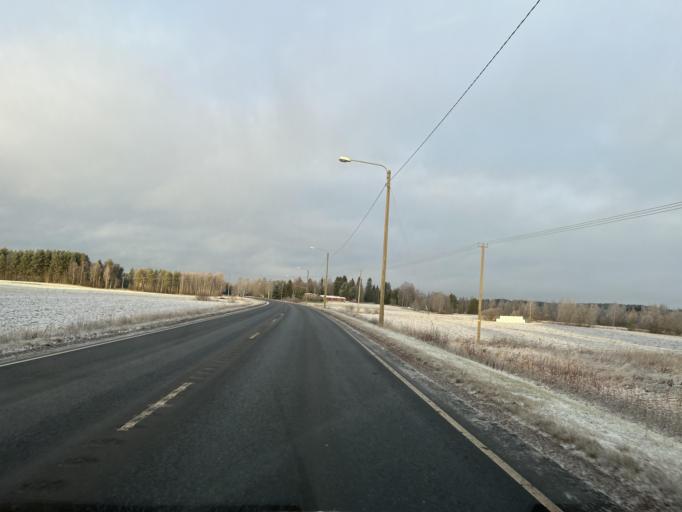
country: FI
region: Northern Ostrobothnia
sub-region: Oulu
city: Muhos
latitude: 64.8596
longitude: 25.8916
